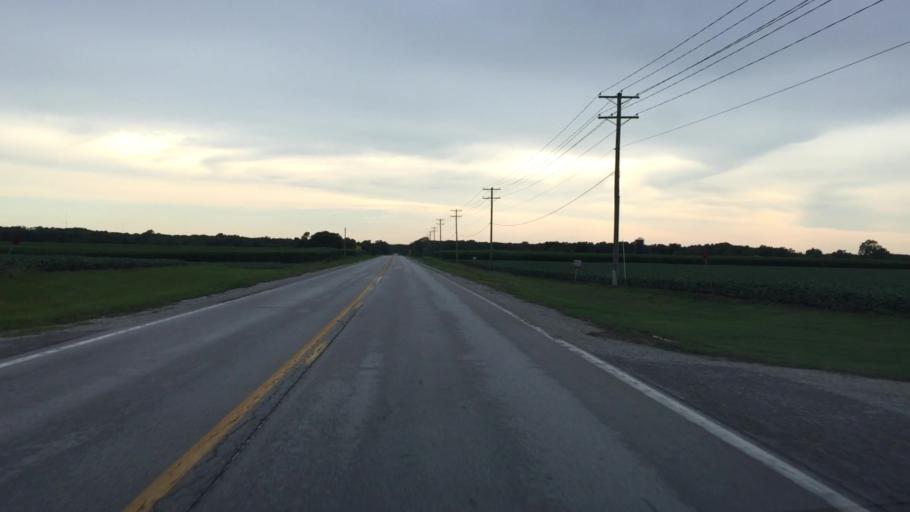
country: US
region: Iowa
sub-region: Lee County
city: Keokuk
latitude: 40.3608
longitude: -91.3648
